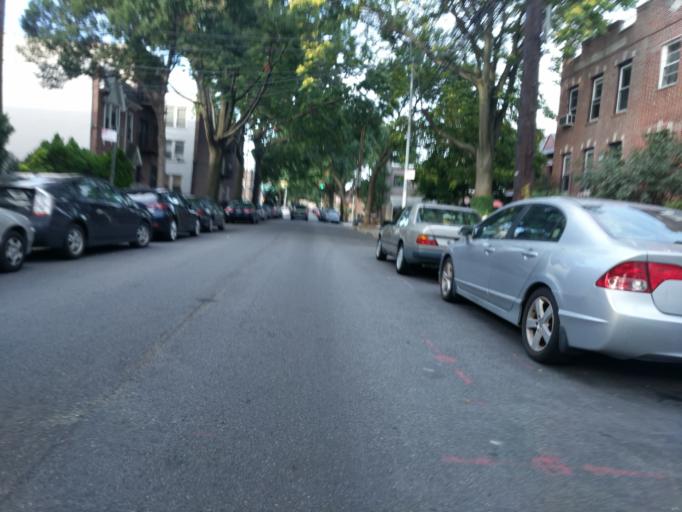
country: US
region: New York
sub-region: Queens County
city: Long Island City
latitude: 40.7755
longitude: -73.9185
